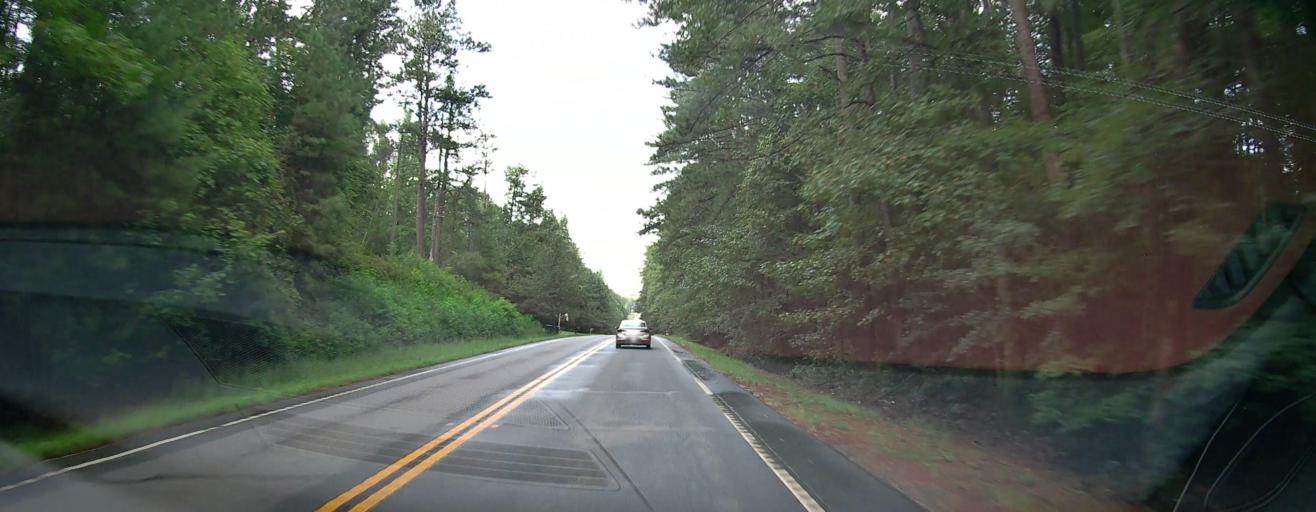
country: US
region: Georgia
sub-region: Coweta County
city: Senoia
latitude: 33.2795
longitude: -84.5511
